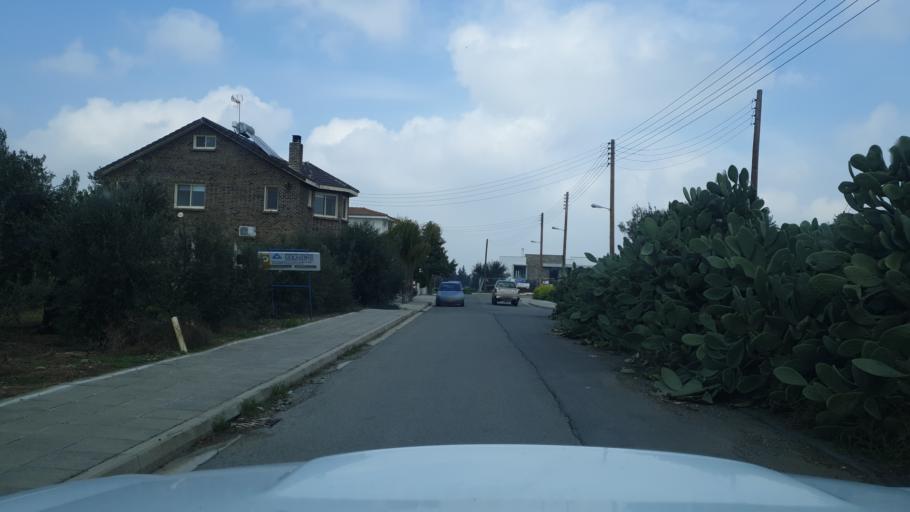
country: CY
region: Lefkosia
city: Kato Deftera
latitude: 35.0870
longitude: 33.2900
